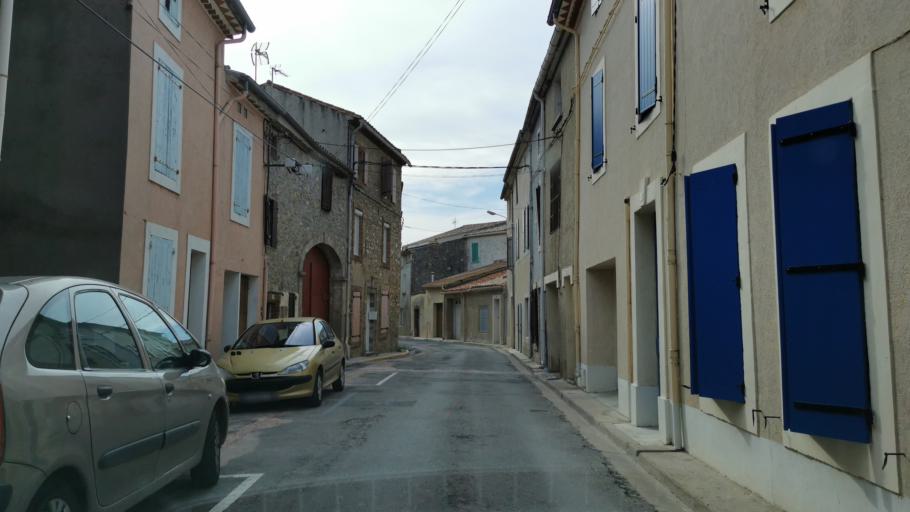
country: FR
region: Languedoc-Roussillon
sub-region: Departement de l'Aude
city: Nevian
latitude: 43.2121
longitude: 2.9053
